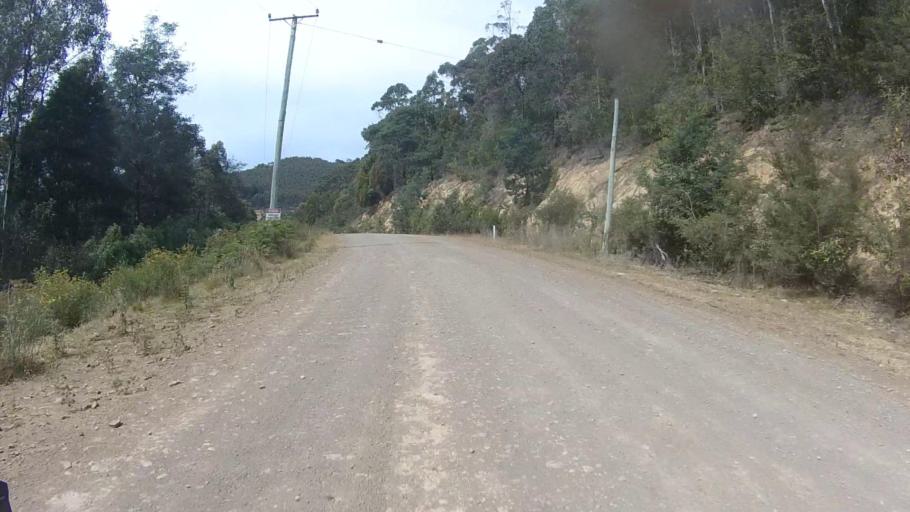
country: AU
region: Tasmania
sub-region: Sorell
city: Sorell
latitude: -42.7711
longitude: 147.8302
